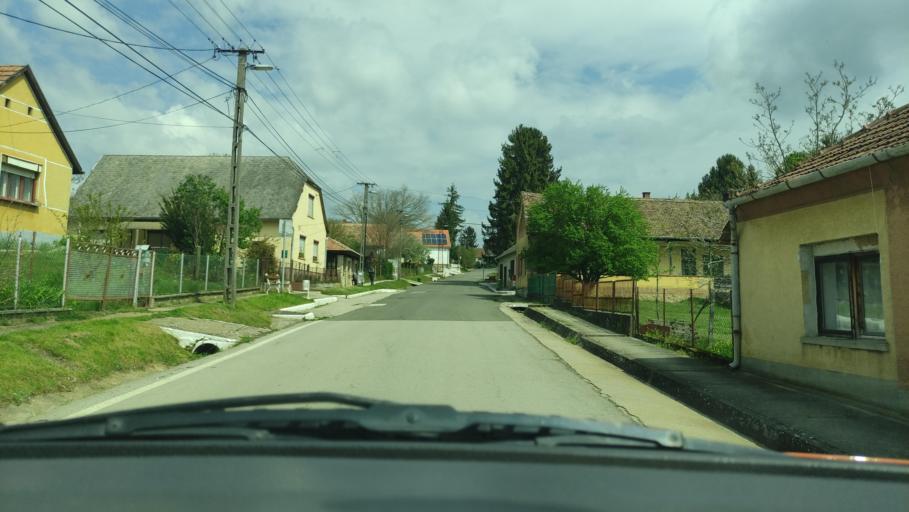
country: HU
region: Baranya
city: Sasd
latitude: 46.2892
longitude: 18.1023
